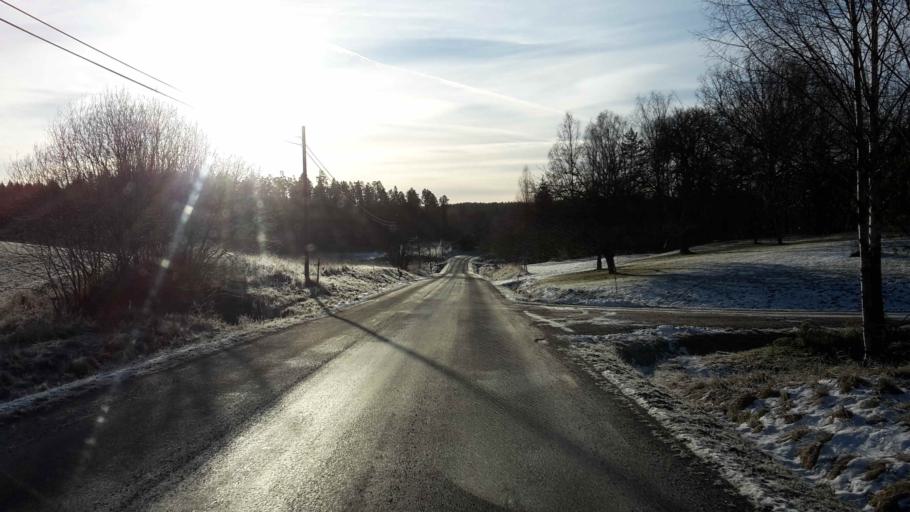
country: SE
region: OEstergoetland
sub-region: Atvidabergs Kommun
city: Atvidaberg
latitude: 58.2230
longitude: 16.0506
